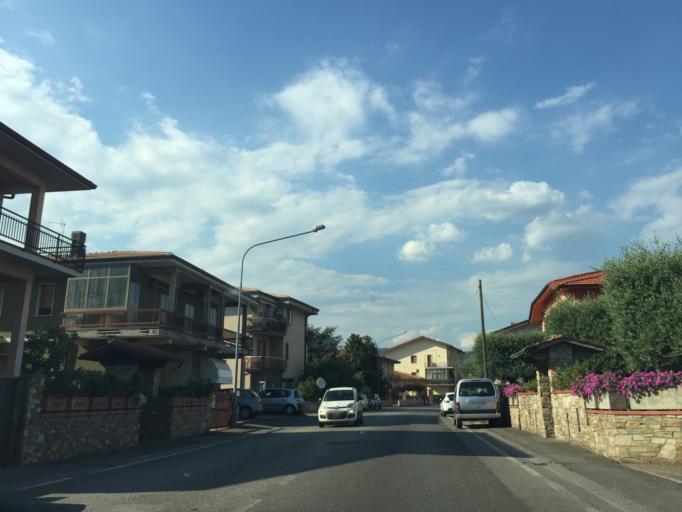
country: IT
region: Tuscany
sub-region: Provincia di Pistoia
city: Pieve a Nievole
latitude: 43.8725
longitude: 10.7993
